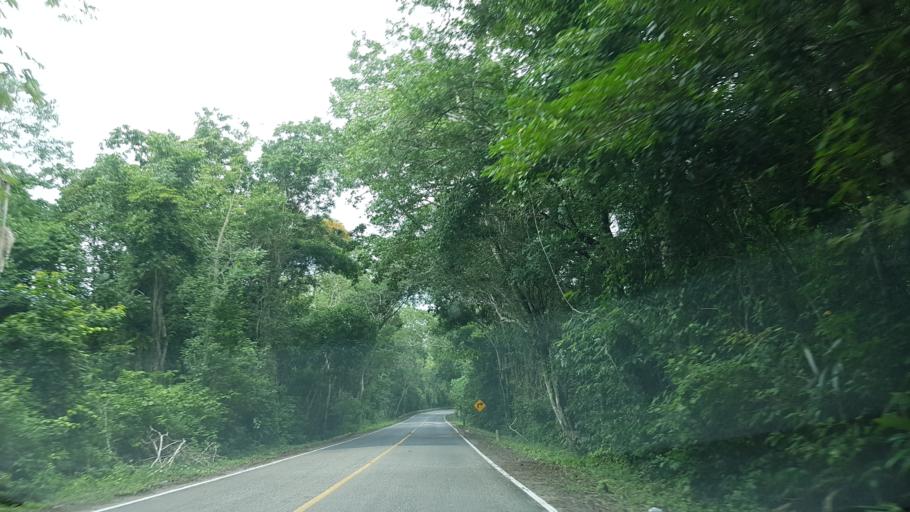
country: GT
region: Peten
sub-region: Municipio de San Jose
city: San Jose
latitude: 17.1734
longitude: -89.6422
